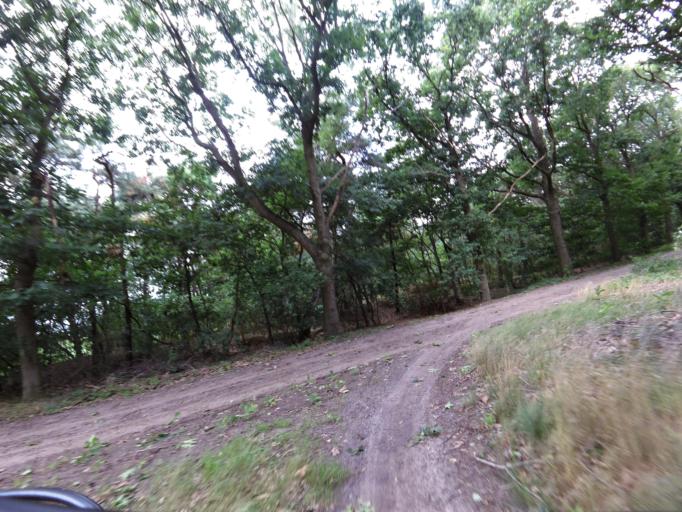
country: NL
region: North Brabant
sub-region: Gemeente Son en Breugel
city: Breugel
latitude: 51.5455
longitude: 5.5045
